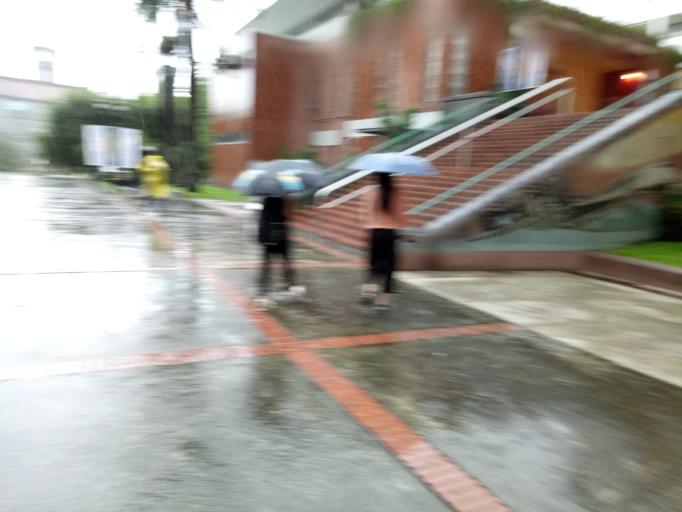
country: TW
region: Taiwan
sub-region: Taichung City
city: Taichung
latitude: 24.0681
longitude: 120.7142
